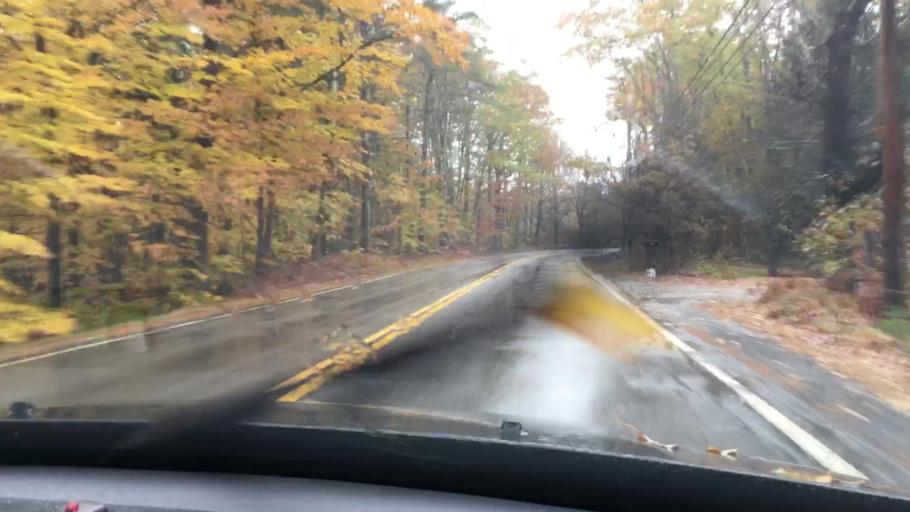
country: US
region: New Hampshire
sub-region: Belknap County
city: Meredith
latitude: 43.7057
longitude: -71.5216
